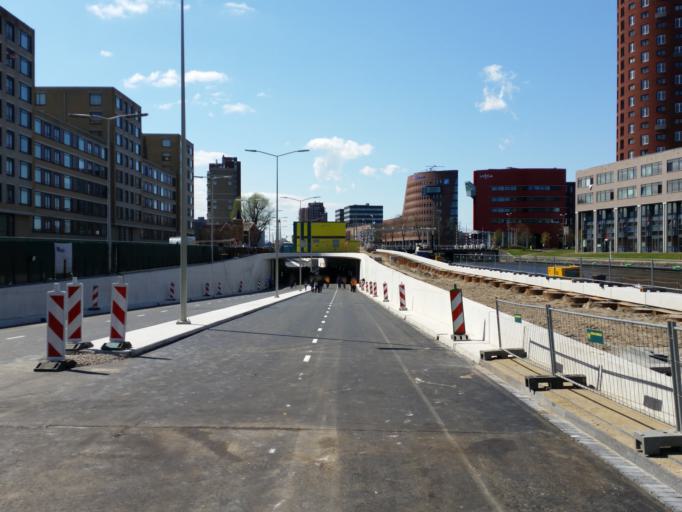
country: NL
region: South Holland
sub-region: Gemeente Den Haag
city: The Hague
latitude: 52.0661
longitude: 4.3253
